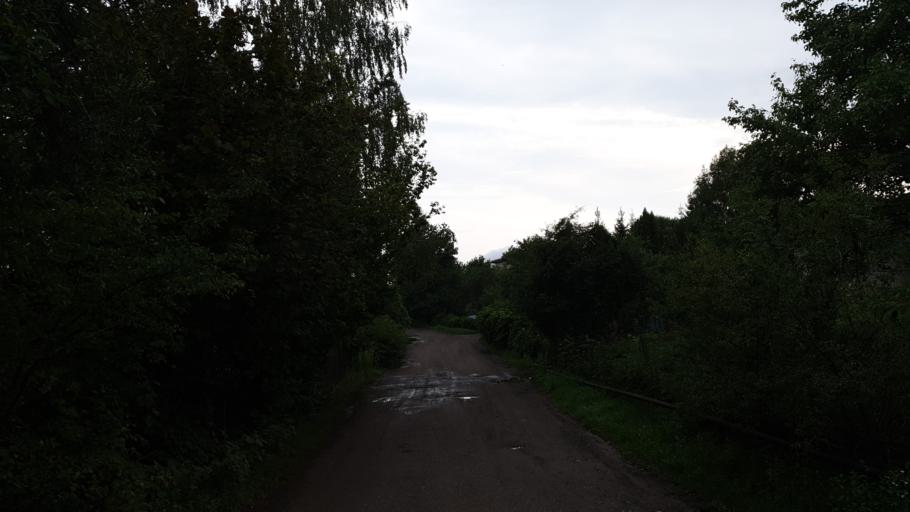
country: LT
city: Grigiskes
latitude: 54.7687
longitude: 25.0154
